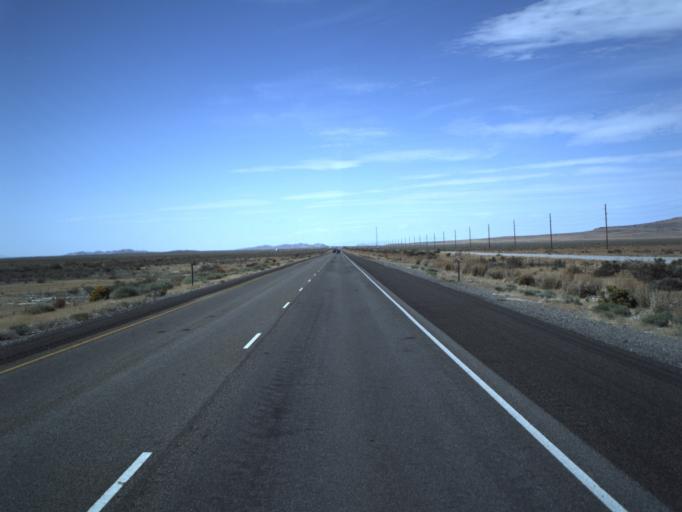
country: US
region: Utah
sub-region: Tooele County
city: Grantsville
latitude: 40.7462
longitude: -113.0637
